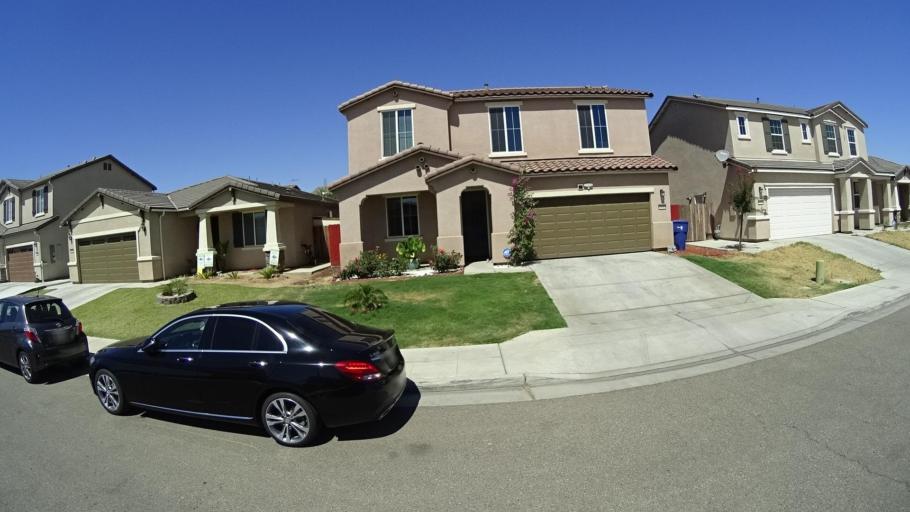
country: US
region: California
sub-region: Fresno County
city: Sunnyside
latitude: 36.7193
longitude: -119.6691
